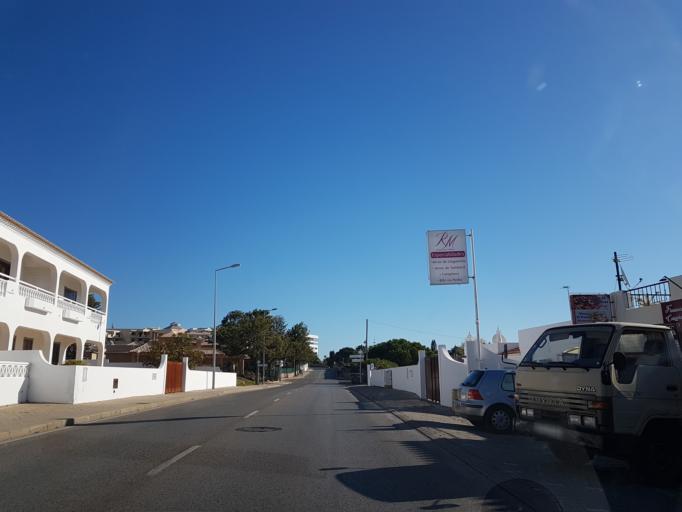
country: PT
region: Faro
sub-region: Albufeira
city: Albufeira
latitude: 37.0912
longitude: -8.2131
